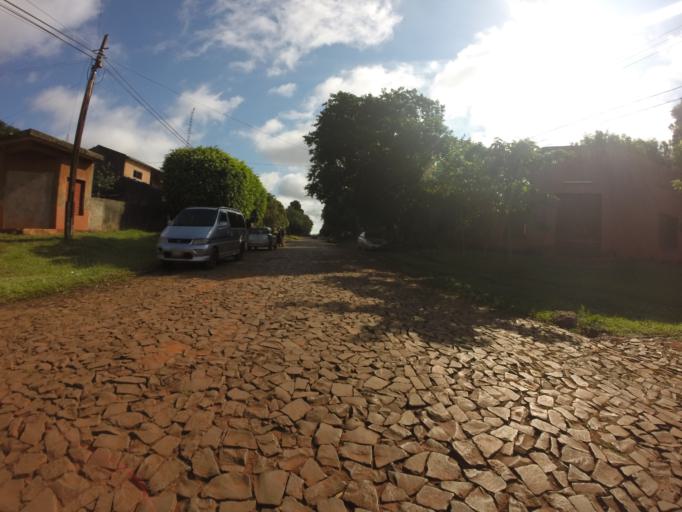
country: PY
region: Alto Parana
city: Ciudad del Este
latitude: -25.4057
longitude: -54.6465
